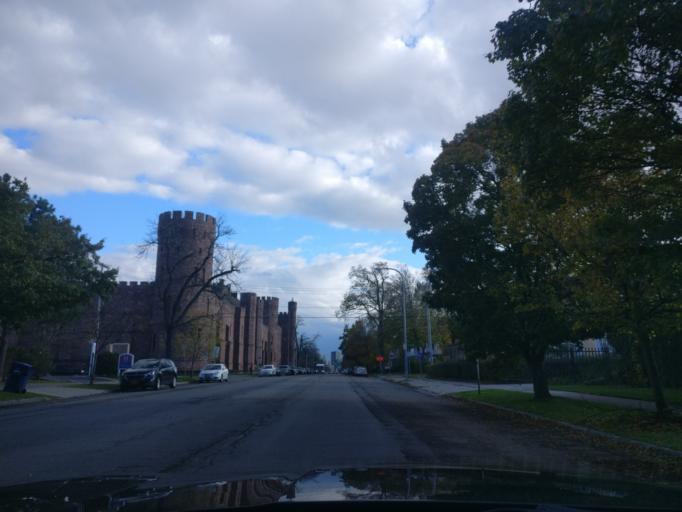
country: US
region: New York
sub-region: Erie County
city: Buffalo
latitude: 42.9049
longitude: -78.8956
